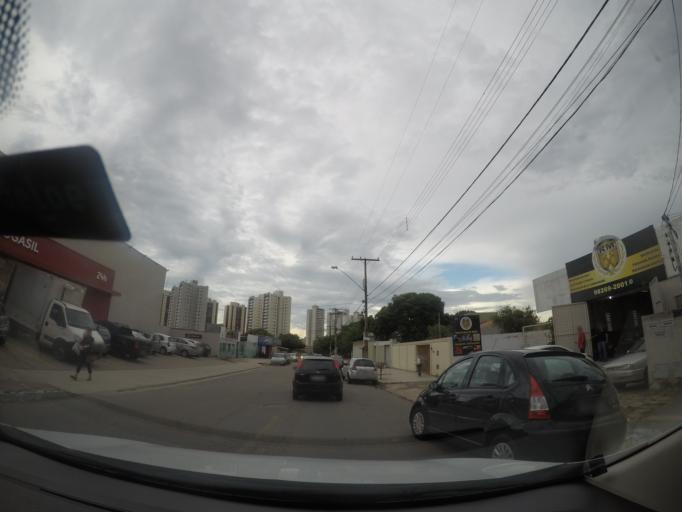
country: BR
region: Goias
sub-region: Goiania
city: Goiania
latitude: -16.6555
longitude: -49.2468
